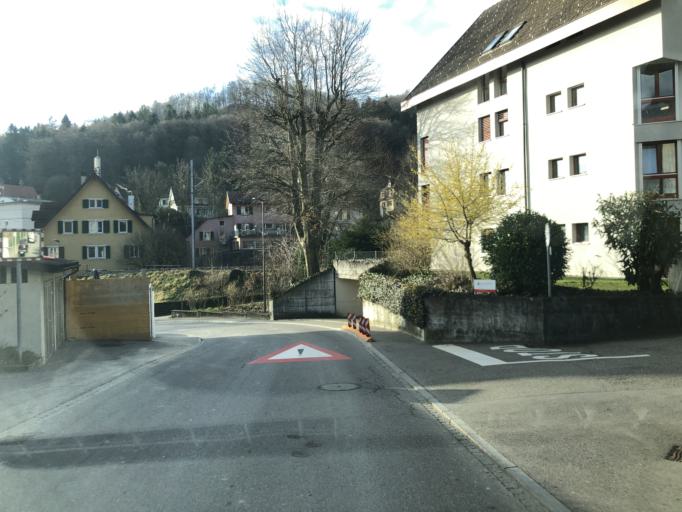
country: CH
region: Aargau
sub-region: Bezirk Baden
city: Baden
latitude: 47.4709
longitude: 8.3017
